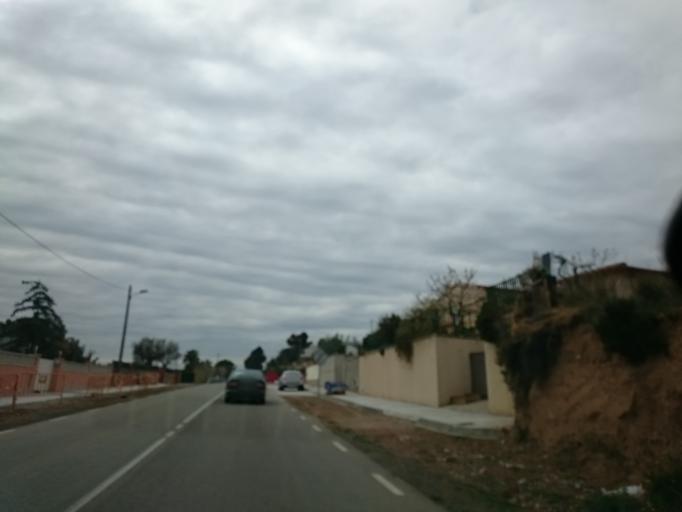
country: ES
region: Catalonia
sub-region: Provincia de Barcelona
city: Piera
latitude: 41.5087
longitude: 1.7305
